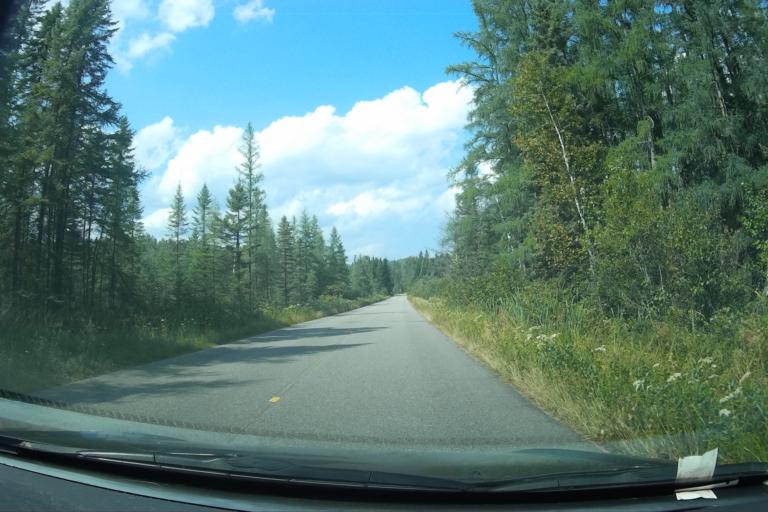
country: CA
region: Ontario
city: Bancroft
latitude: 45.6269
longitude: -78.3513
